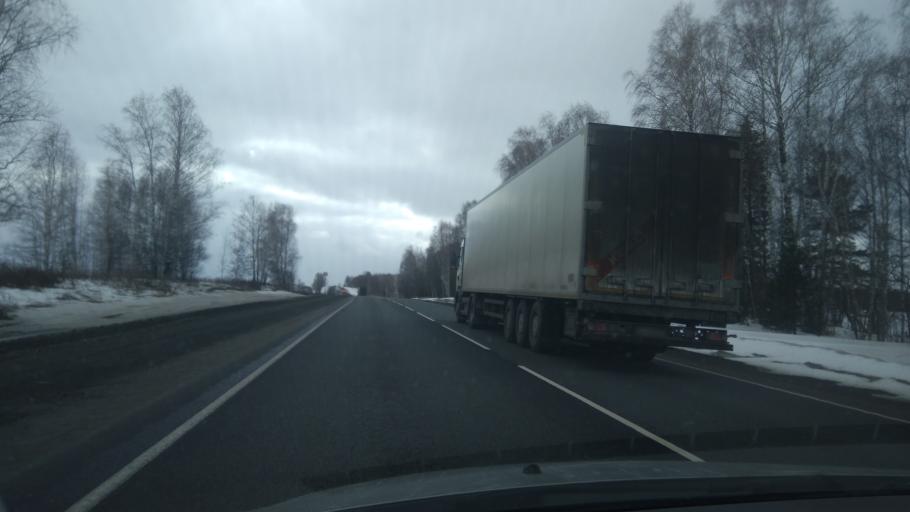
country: RU
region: Perm
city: Suksun
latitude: 56.9683
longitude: 57.5189
